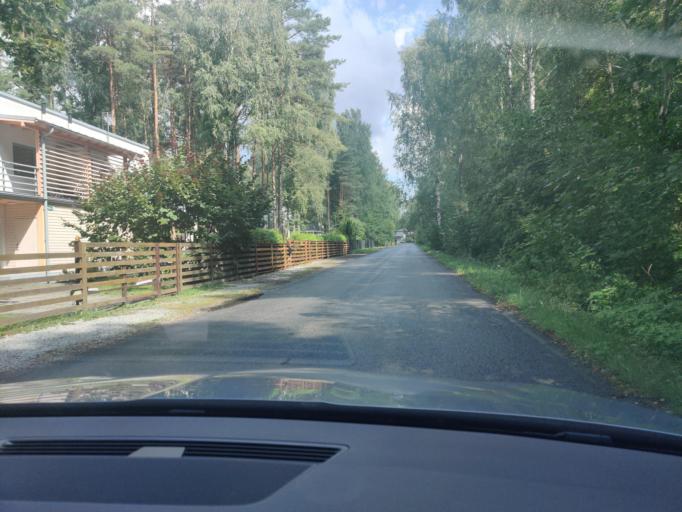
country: EE
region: Harju
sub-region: Saue vald
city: Laagri
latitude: 59.3578
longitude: 24.6232
